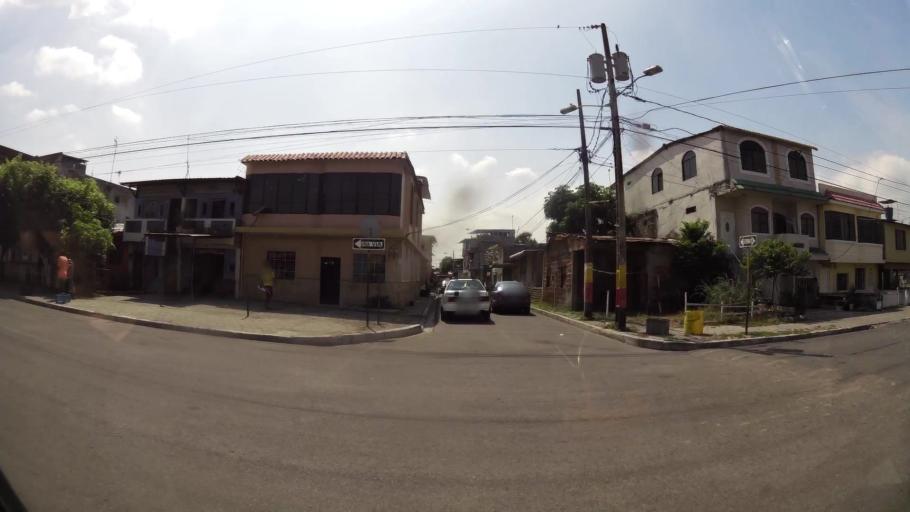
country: EC
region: Guayas
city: Eloy Alfaro
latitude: -2.1537
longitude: -79.8383
